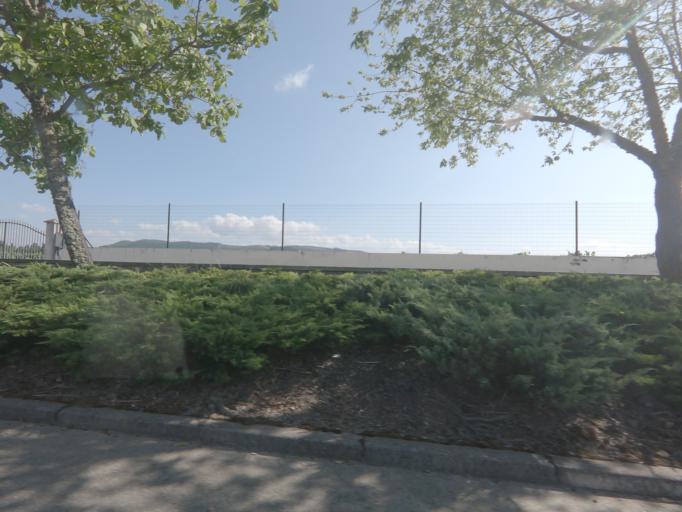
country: PT
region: Vila Real
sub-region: Sabrosa
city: Sabrosa
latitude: 41.2629
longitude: -7.5883
